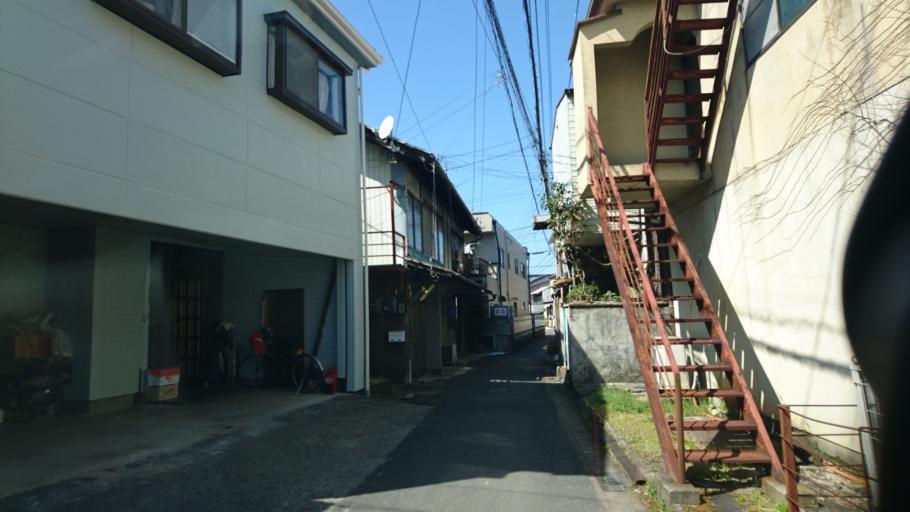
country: JP
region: Gifu
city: Nakatsugawa
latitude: 35.4537
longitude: 137.4104
